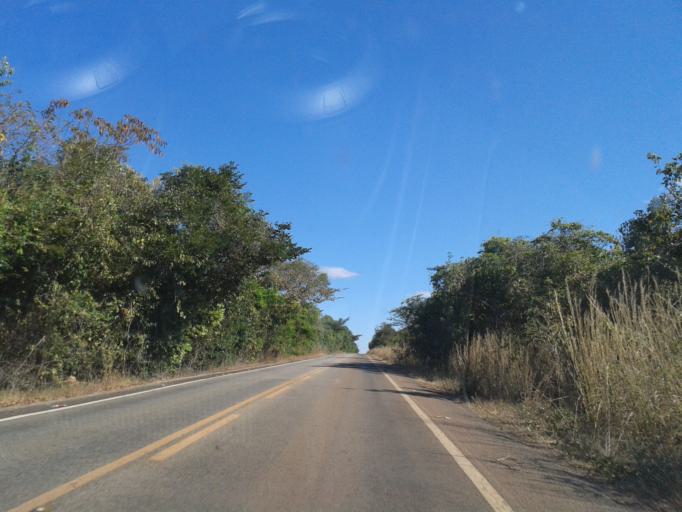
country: BR
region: Goias
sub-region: Mozarlandia
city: Mozarlandia
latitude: -14.4335
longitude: -50.4557
